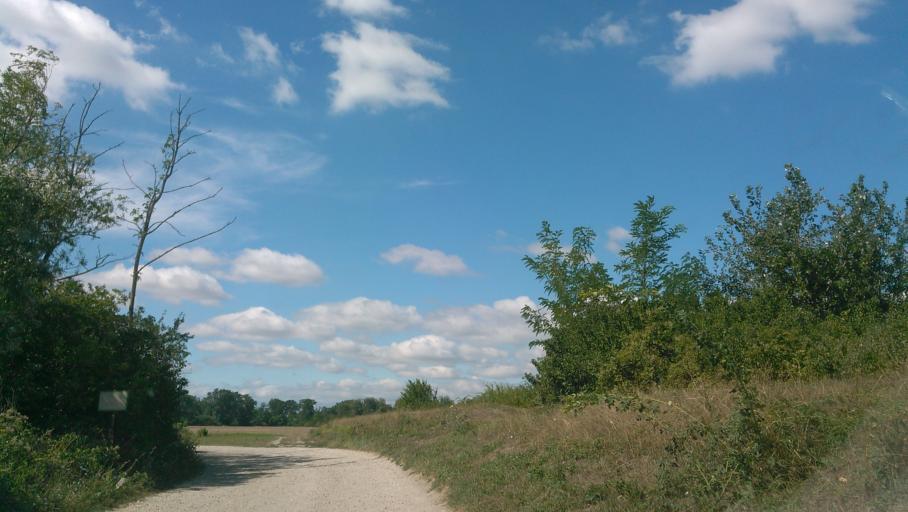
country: SK
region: Trnavsky
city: Sladkovicovo
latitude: 48.1923
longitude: 17.5863
